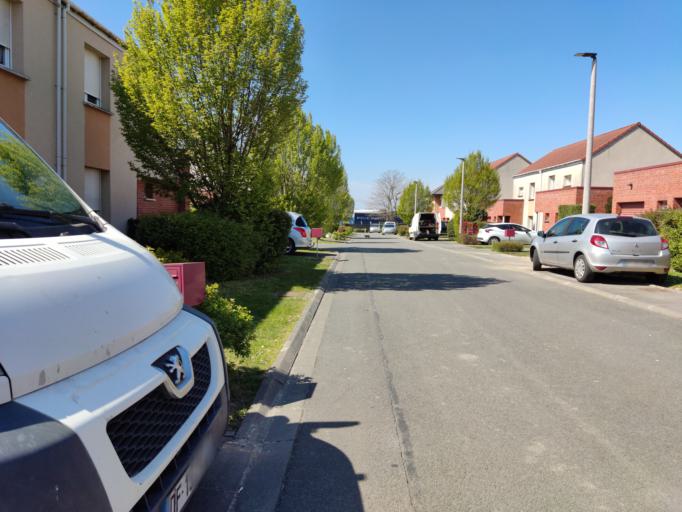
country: FR
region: Nord-Pas-de-Calais
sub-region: Departement du Pas-de-Calais
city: Henin-Beaumont
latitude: 50.4022
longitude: 2.9654
